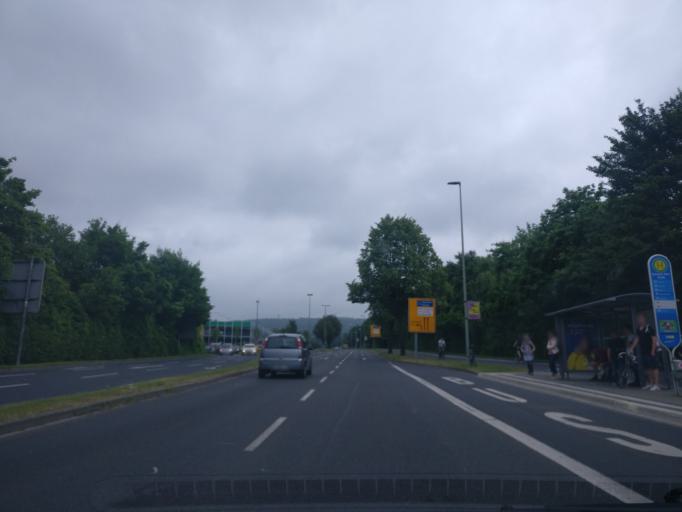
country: DE
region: Lower Saxony
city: Goettingen
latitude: 51.5537
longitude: 9.9406
